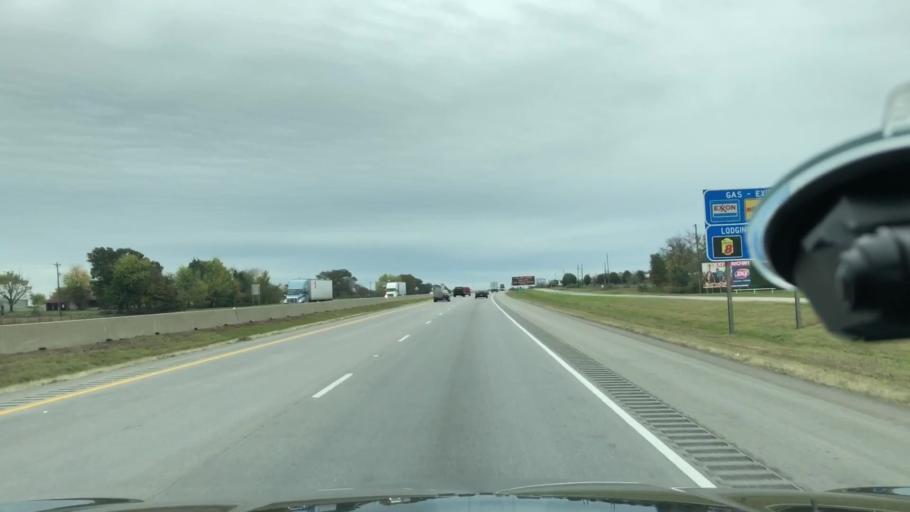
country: US
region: Texas
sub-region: Franklin County
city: Mount Vernon
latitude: 33.1629
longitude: -95.2512
